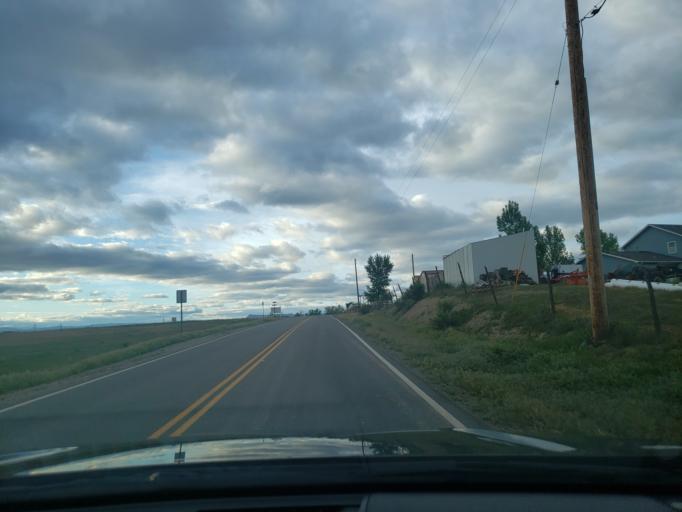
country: US
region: Colorado
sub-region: Mesa County
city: Fruita
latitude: 39.1852
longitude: -108.7291
